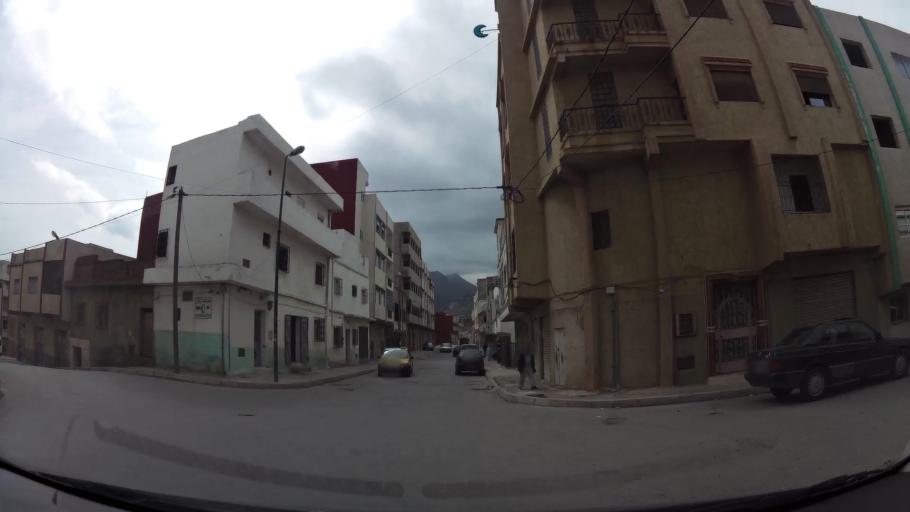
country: MA
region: Tanger-Tetouan
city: Tetouan
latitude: 35.5692
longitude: -5.3958
